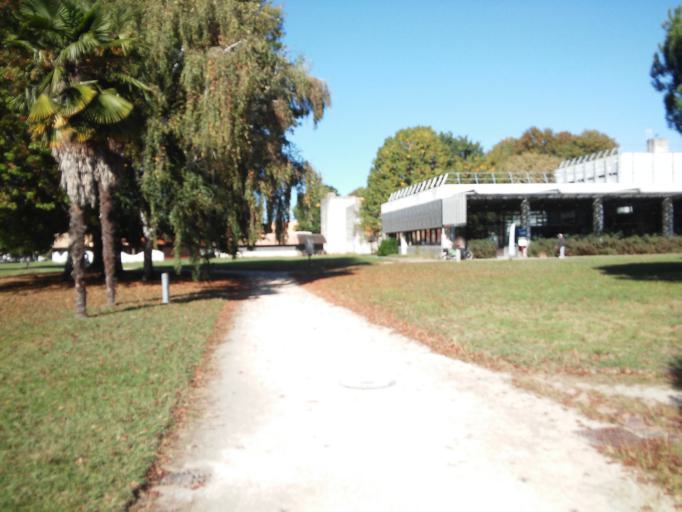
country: FR
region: Aquitaine
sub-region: Departement des Pyrenees-Atlantiques
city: Pau
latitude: 43.3137
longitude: -0.3657
